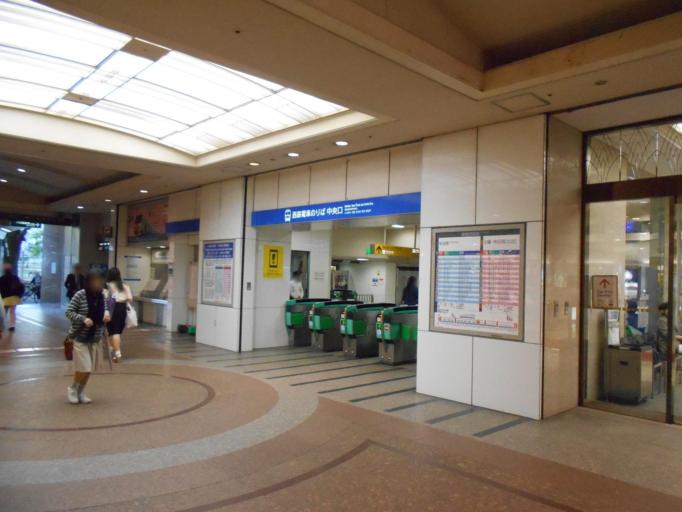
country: JP
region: Fukuoka
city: Fukuoka-shi
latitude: 33.5886
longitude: 130.4001
